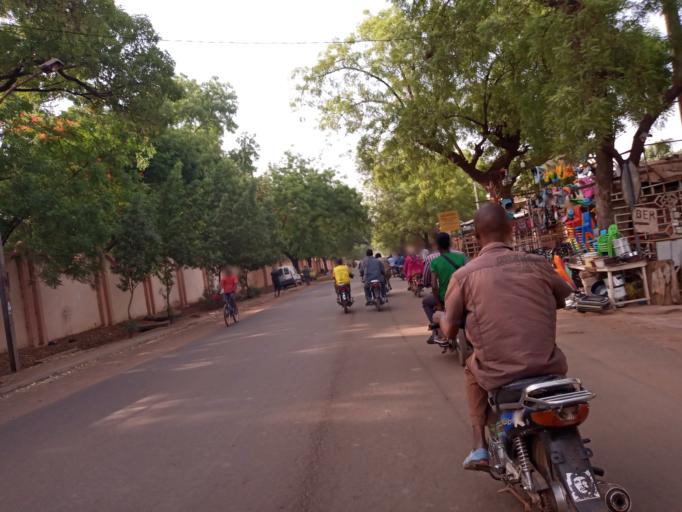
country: ML
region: Bamako
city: Bamako
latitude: 12.6569
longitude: -7.9802
